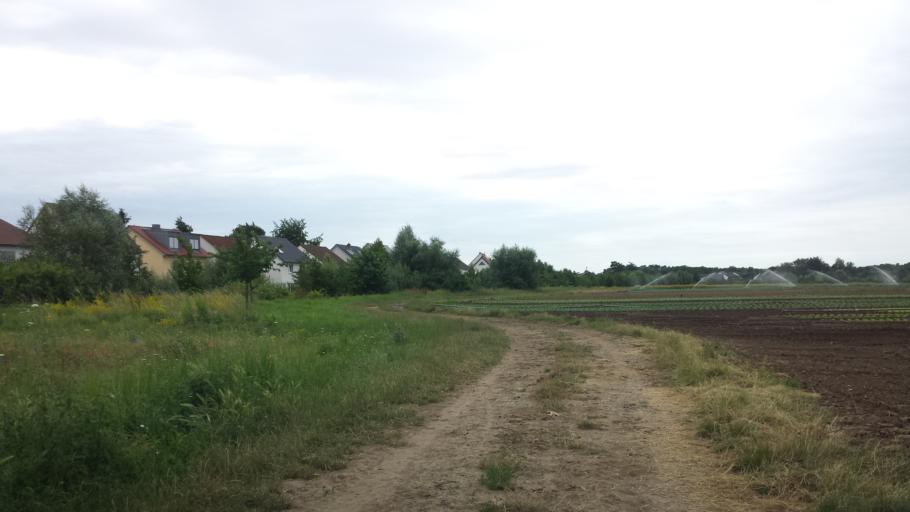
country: DE
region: Rheinland-Pfalz
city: Lambsheim
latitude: 49.5062
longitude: 8.2883
